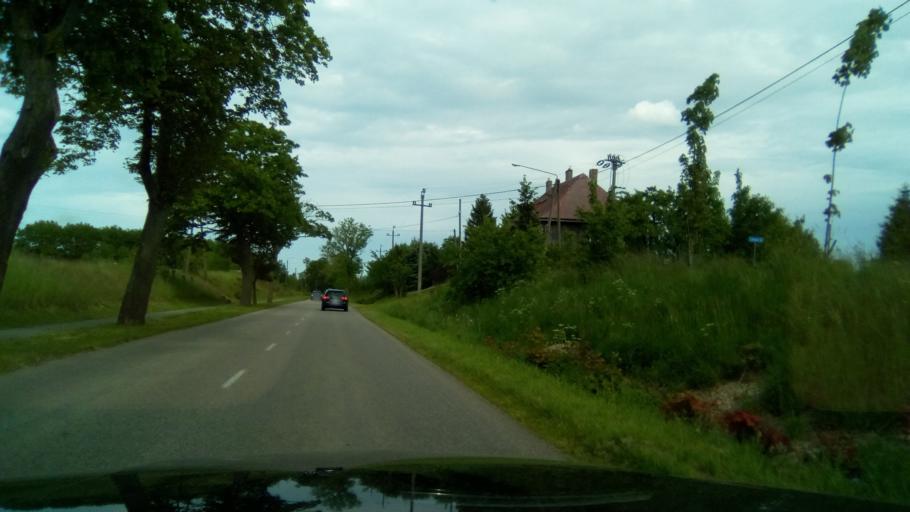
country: PL
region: Pomeranian Voivodeship
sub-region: Powiat pucki
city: Wierzchucino
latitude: 54.7886
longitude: 18.0072
